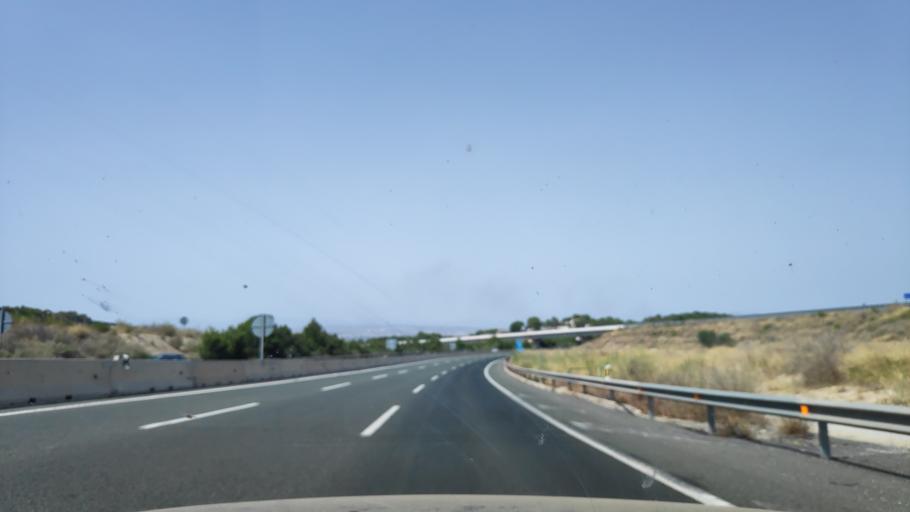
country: ES
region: Murcia
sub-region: Murcia
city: Alcantarilla
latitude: 37.9156
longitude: -1.1648
